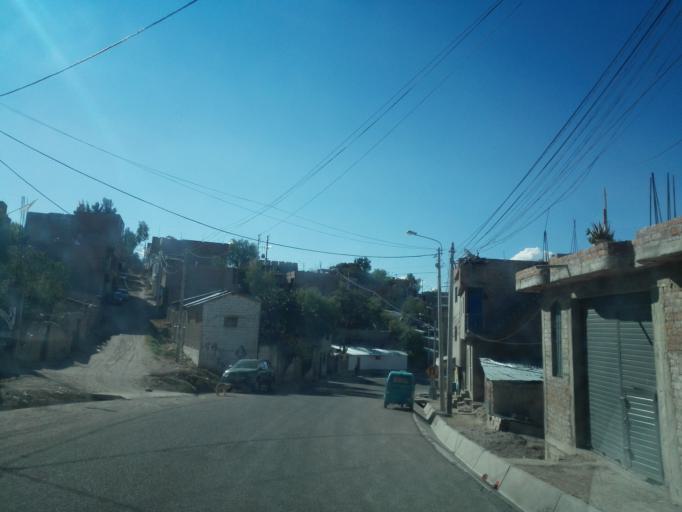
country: PE
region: Ayacucho
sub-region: Provincia de Huamanga
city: Ayacucho
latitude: -13.1455
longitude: -74.2165
